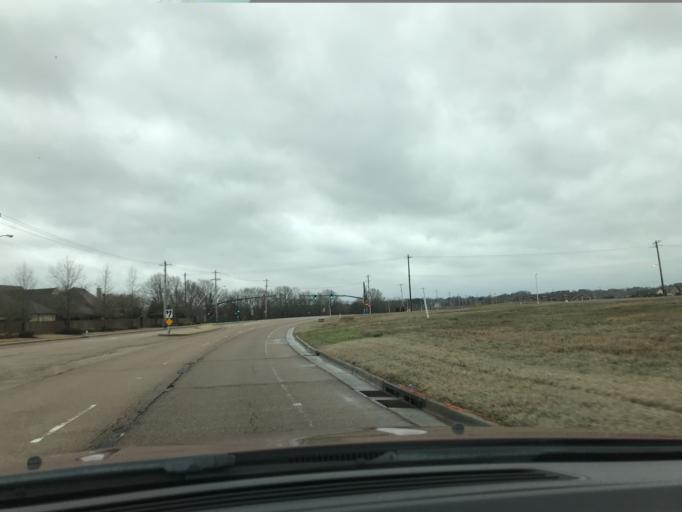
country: US
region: Tennessee
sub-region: Shelby County
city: Collierville
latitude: 35.0834
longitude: -89.6823
